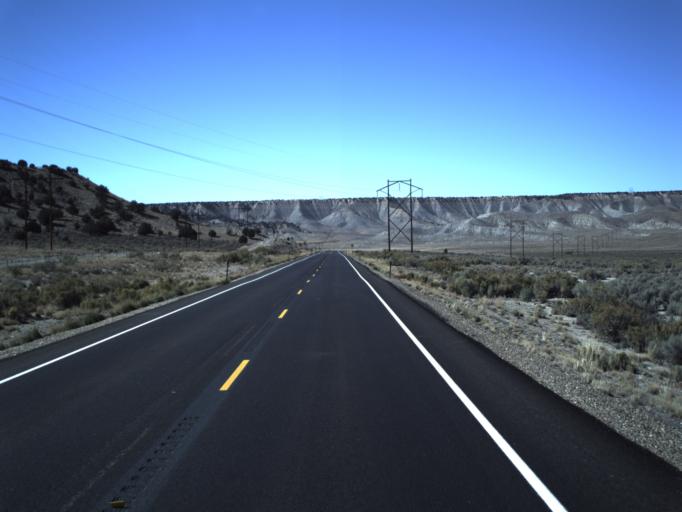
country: US
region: Utah
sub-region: Garfield County
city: Panguitch
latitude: 37.5997
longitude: -111.9545
